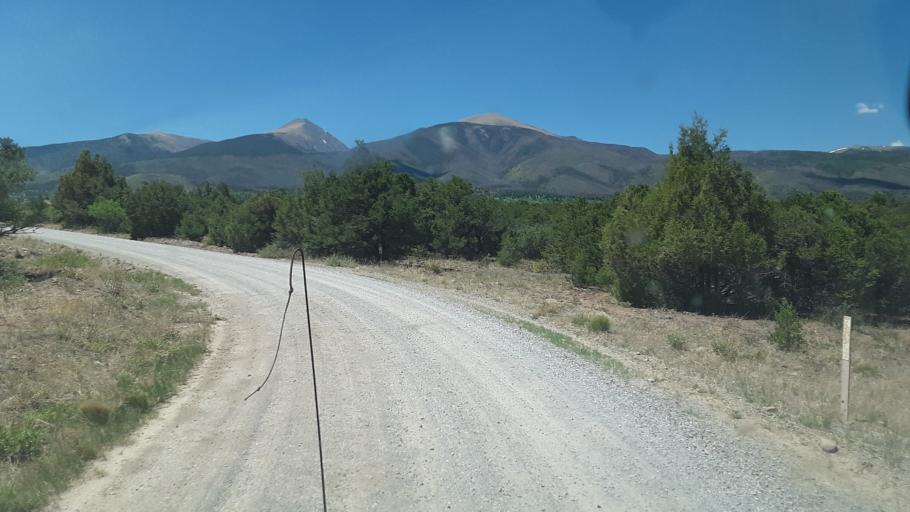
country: US
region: Colorado
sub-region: Custer County
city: Westcliffe
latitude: 38.3117
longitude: -105.6739
